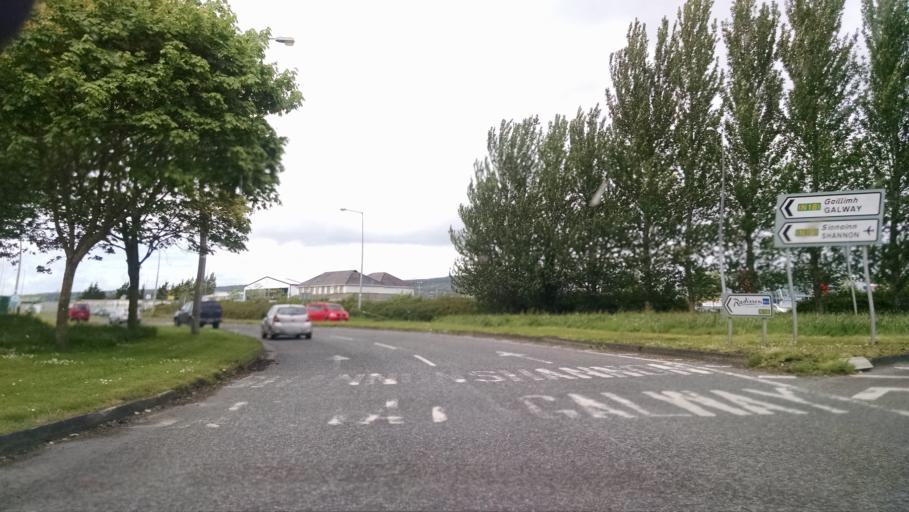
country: IE
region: Munster
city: Moyross
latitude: 52.6741
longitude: -8.6753
